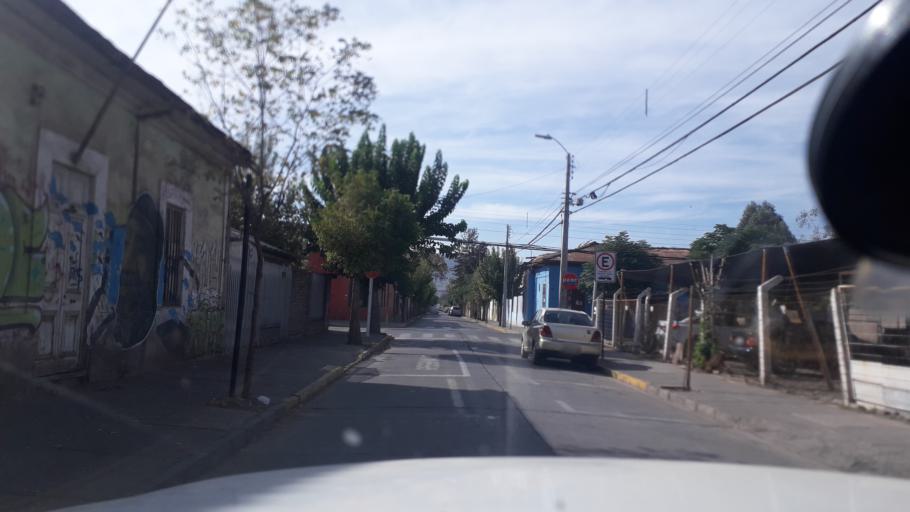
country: CL
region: Valparaiso
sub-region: Provincia de San Felipe
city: San Felipe
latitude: -32.7486
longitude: -70.7279
